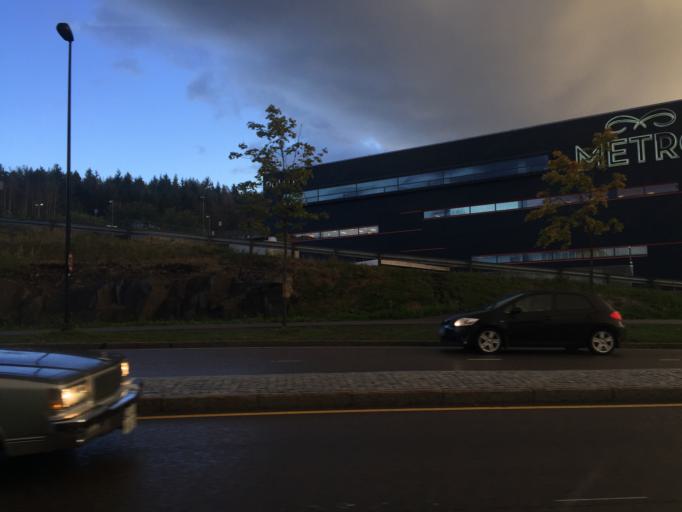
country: NO
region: Akershus
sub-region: Lorenskog
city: Kjenn
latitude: 59.9283
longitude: 10.9636
